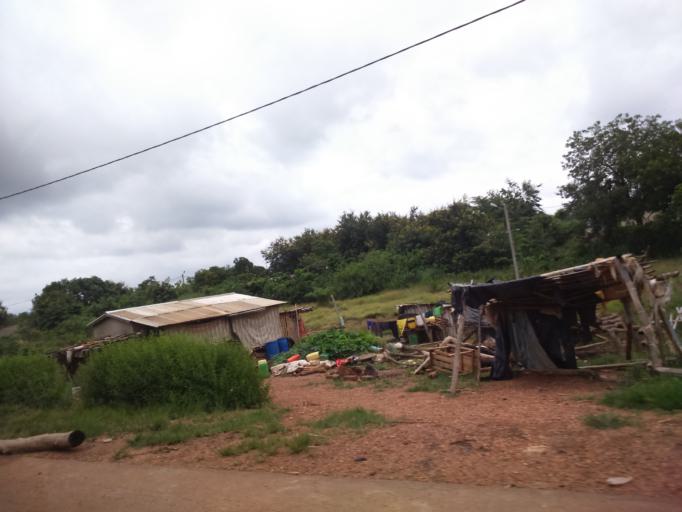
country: CI
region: Moyen-Comoe
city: Abengourou
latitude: 6.6332
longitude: -3.7101
